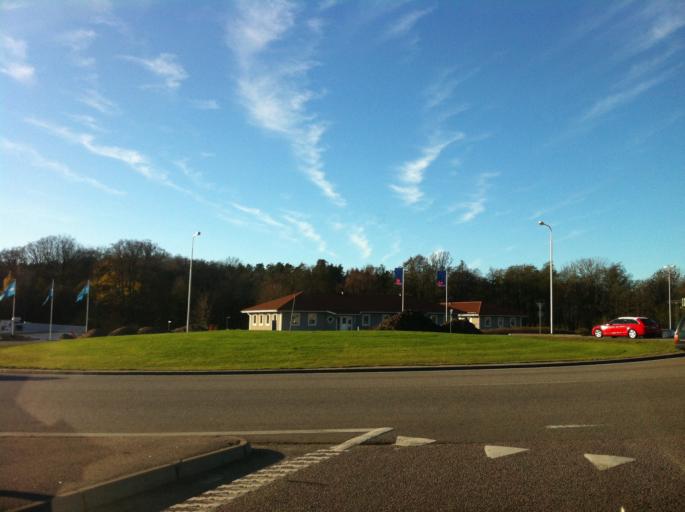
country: SE
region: Blekinge
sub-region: Karlshamns Kommun
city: Karlshamn
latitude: 56.1893
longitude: 14.8583
